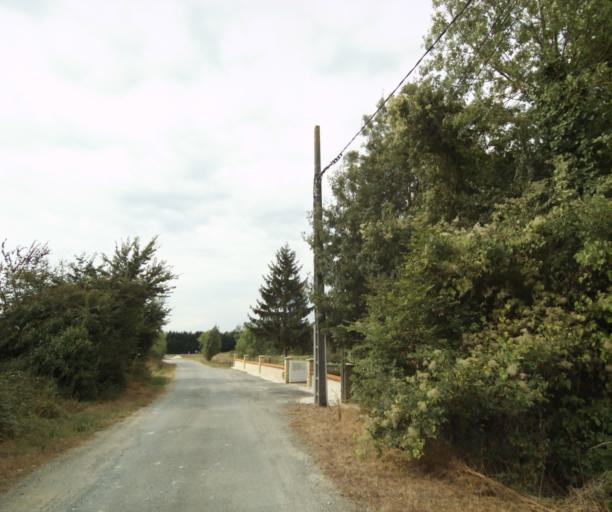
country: FR
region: Poitou-Charentes
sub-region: Departement de la Charente-Maritime
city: Tonnay-Charente
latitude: 45.9536
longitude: -0.8718
